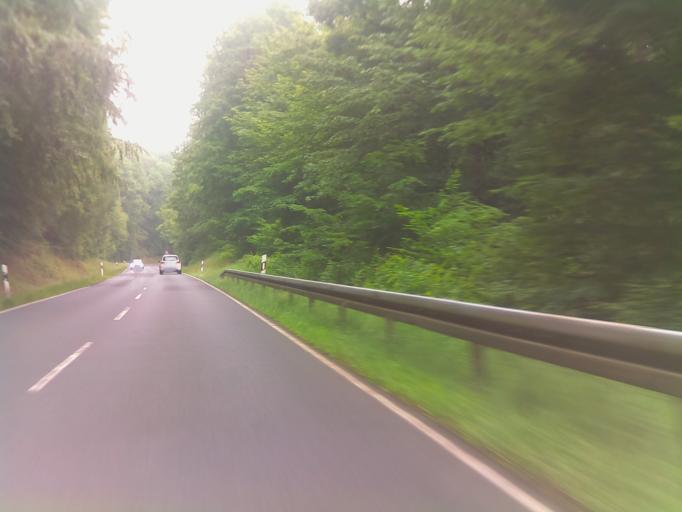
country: DE
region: Hesse
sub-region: Regierungsbezirk Darmstadt
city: Steinau an der Strasse
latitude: 50.2513
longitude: 9.4359
